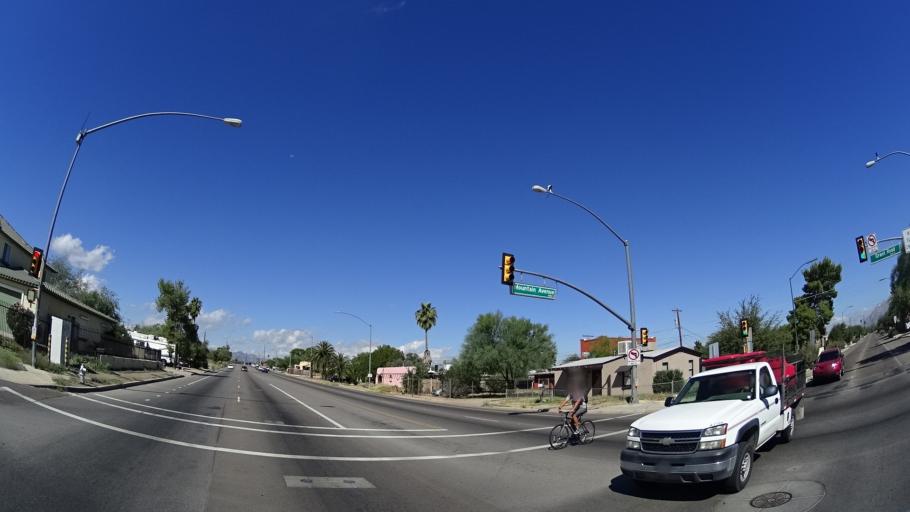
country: US
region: Arizona
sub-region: Pima County
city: Tucson
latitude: 32.2498
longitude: -110.9525
